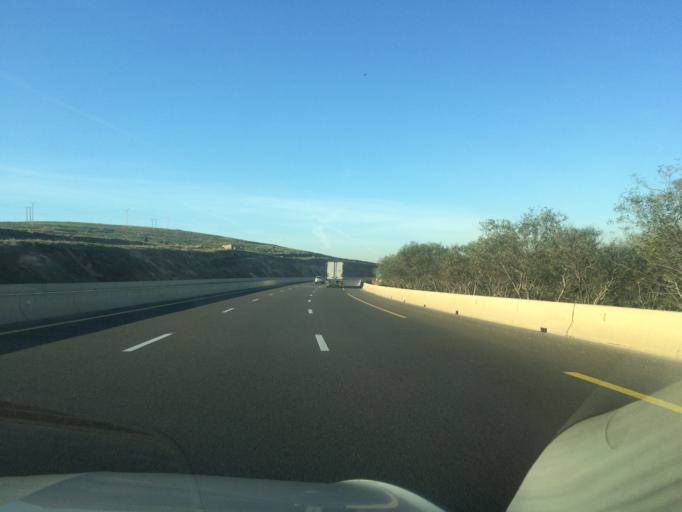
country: DZ
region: Chlef
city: Boukadir
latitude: 36.0695
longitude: 1.1677
